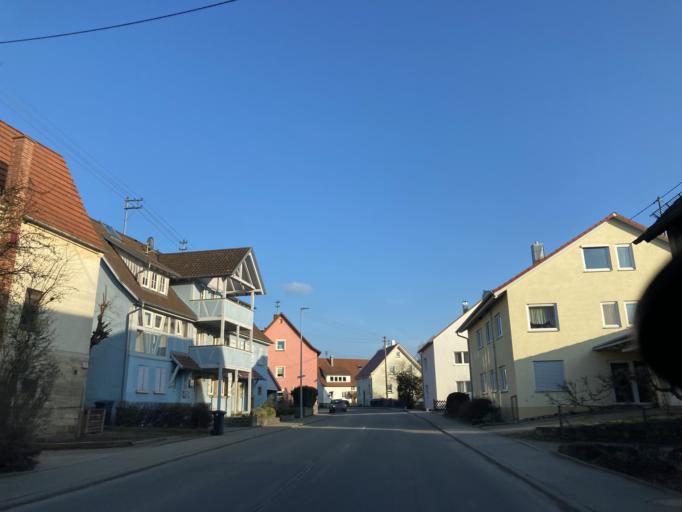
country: DE
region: Baden-Wuerttemberg
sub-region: Tuebingen Region
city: Rottenburg
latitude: 48.4355
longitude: 8.9373
